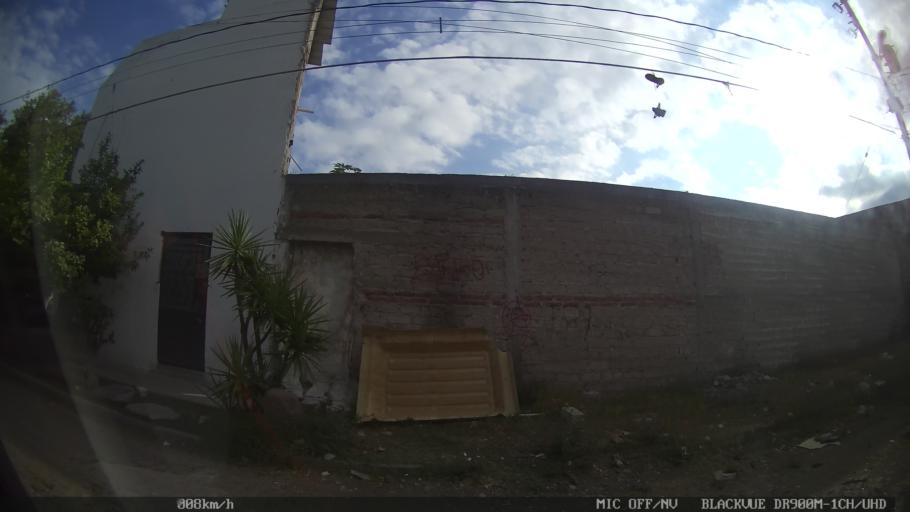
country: MX
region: Jalisco
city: Tonala
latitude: 20.6735
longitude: -103.2398
